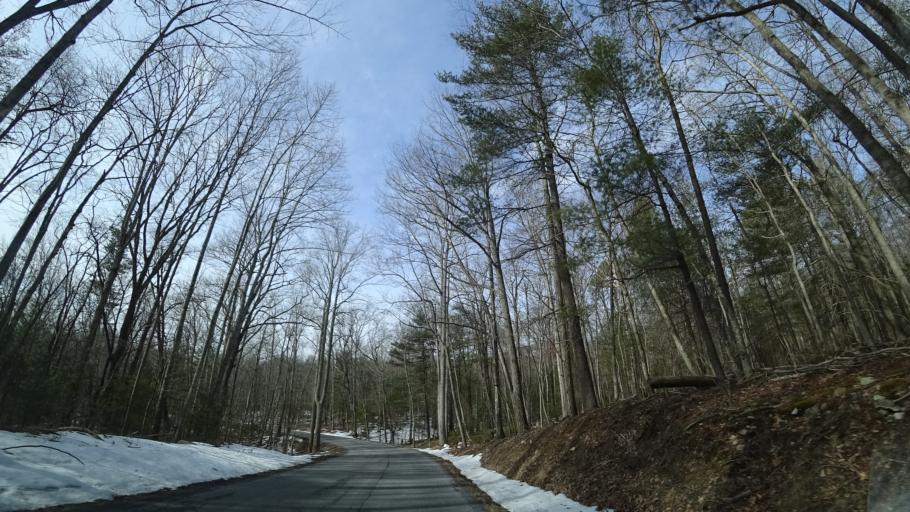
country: US
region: Virginia
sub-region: Shenandoah County
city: Edinburg
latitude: 38.9549
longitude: -78.6872
